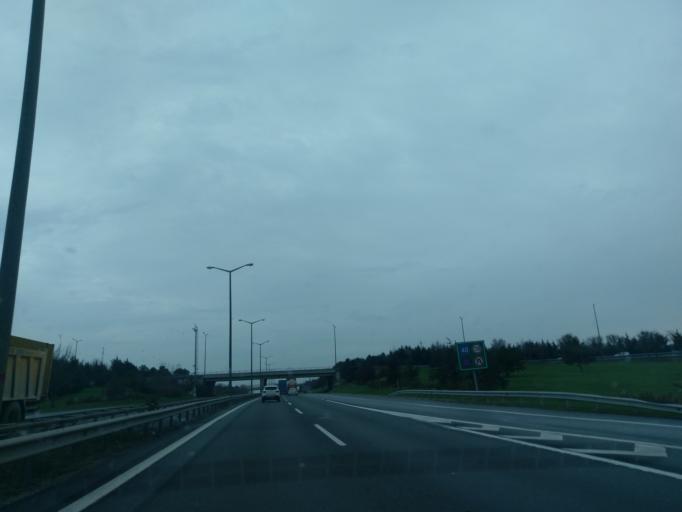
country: TR
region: Istanbul
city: Silivri
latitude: 41.1106
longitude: 28.2663
